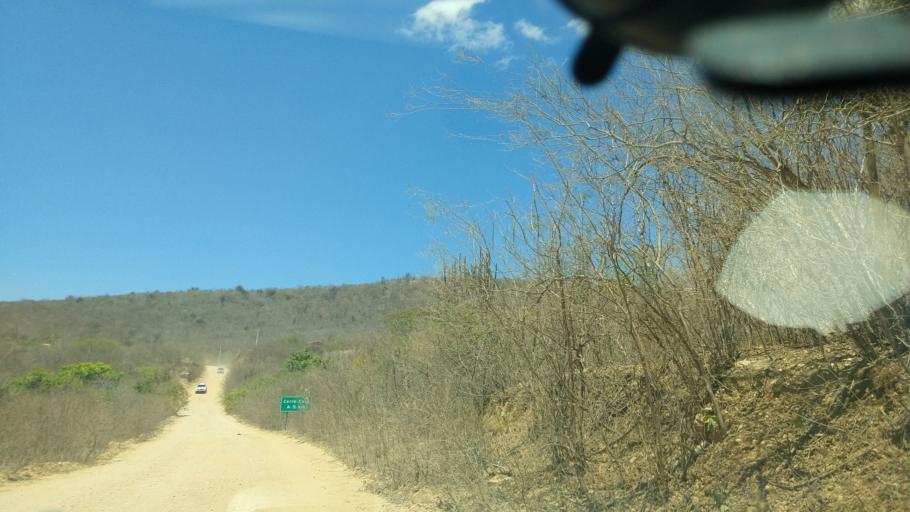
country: BR
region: Rio Grande do Norte
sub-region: Cerro Cora
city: Cerro Cora
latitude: -6.0133
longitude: -36.3157
